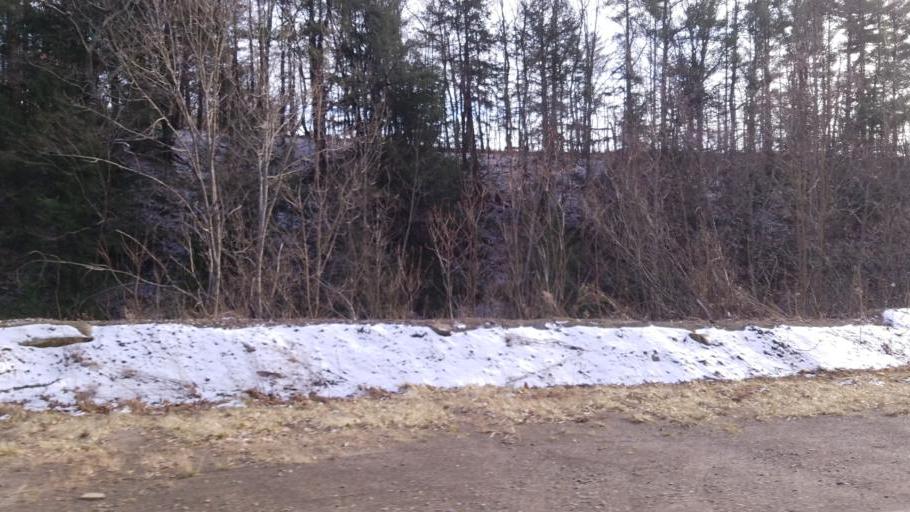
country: US
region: New York
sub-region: Allegany County
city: Wellsville
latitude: 42.1726
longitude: -77.9374
